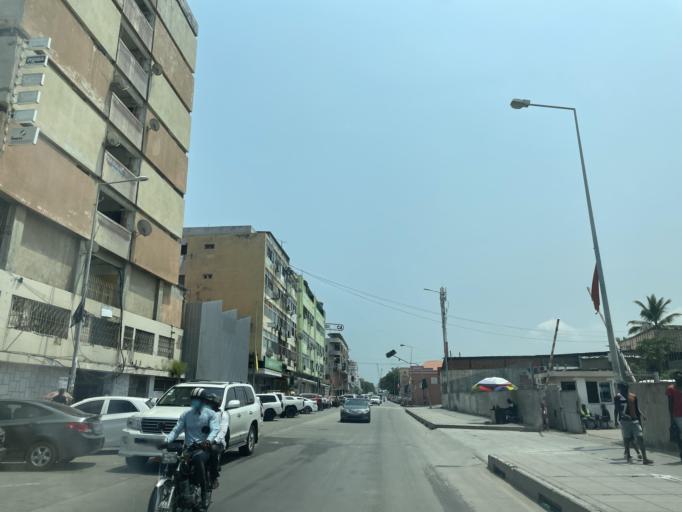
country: AO
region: Luanda
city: Luanda
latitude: -8.8076
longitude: 13.2407
